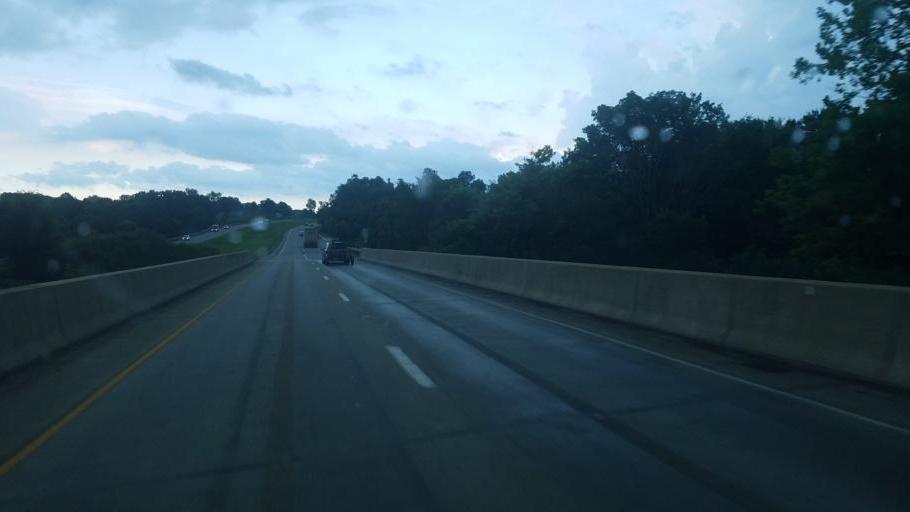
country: US
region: Pennsylvania
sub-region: Butler County
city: Slippery Rock
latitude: 41.0366
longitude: -80.1240
